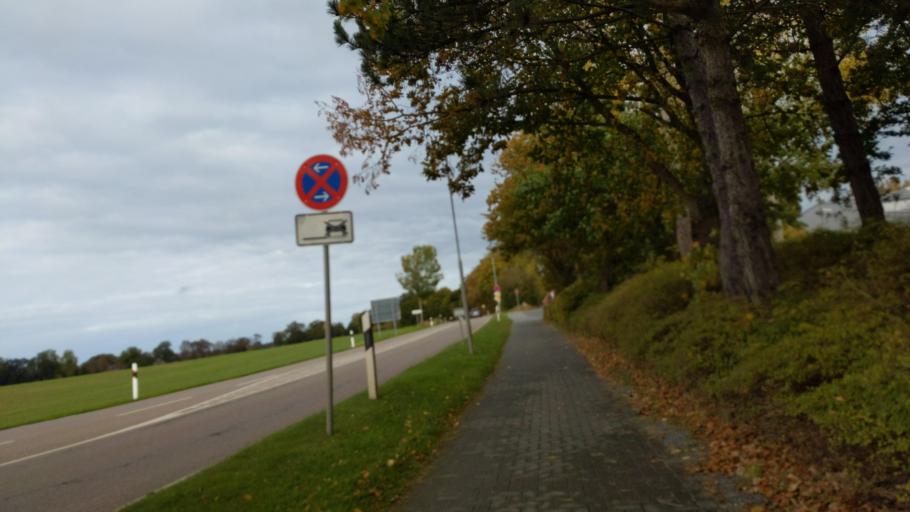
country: DE
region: Schleswig-Holstein
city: Sierksdorf
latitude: 54.0756
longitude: 10.7768
